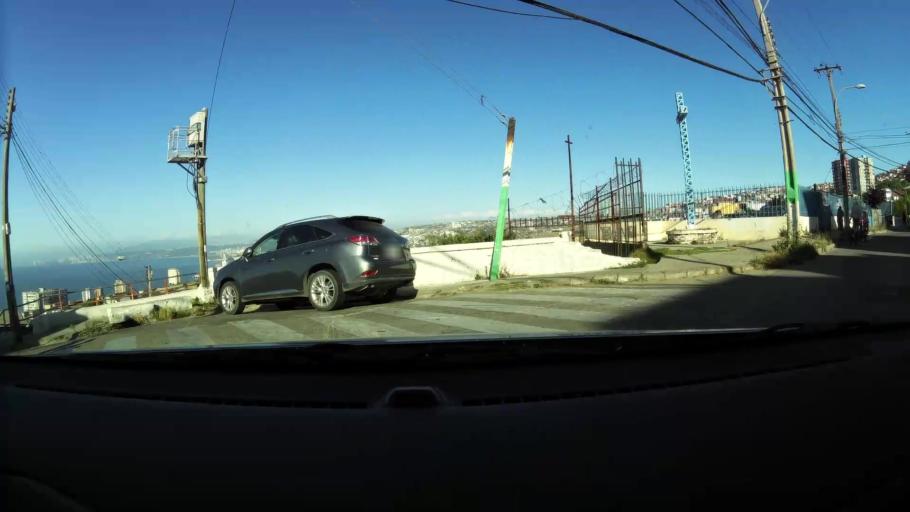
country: CL
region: Valparaiso
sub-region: Provincia de Valparaiso
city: Valparaiso
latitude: -33.0519
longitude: -71.6264
